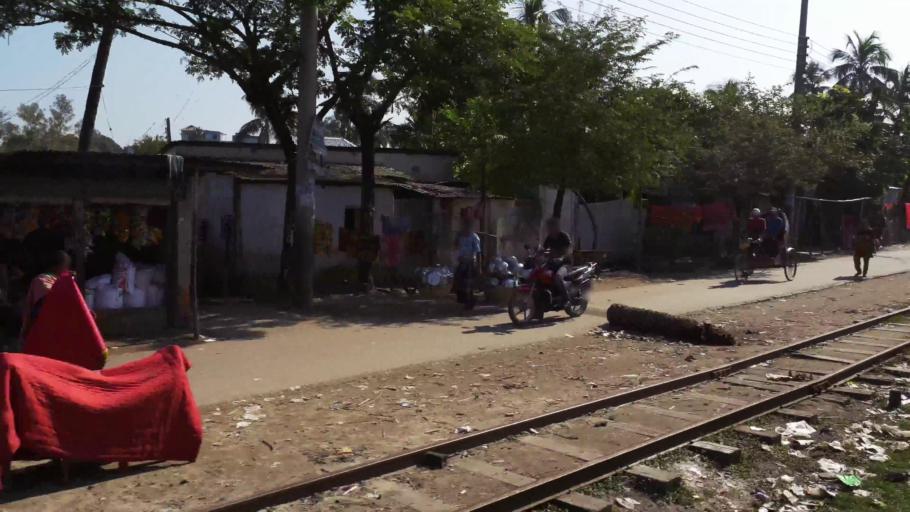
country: BD
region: Dhaka
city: Mymensingh
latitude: 24.6217
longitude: 90.4730
